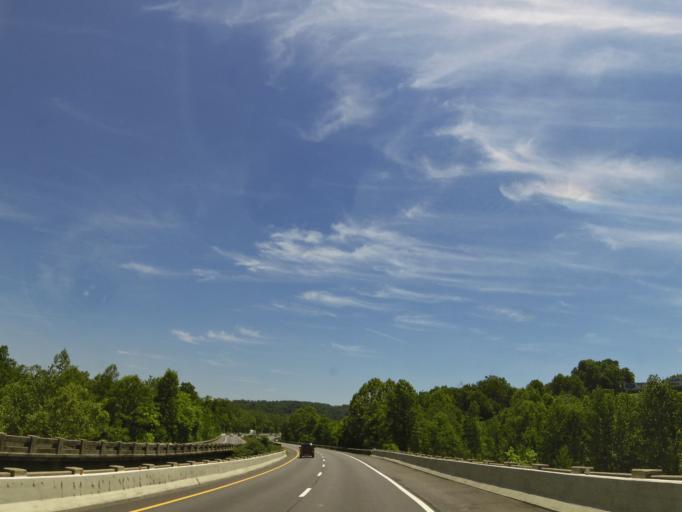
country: US
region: Tennessee
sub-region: Campbell County
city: Caryville
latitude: 36.3068
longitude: -84.2298
